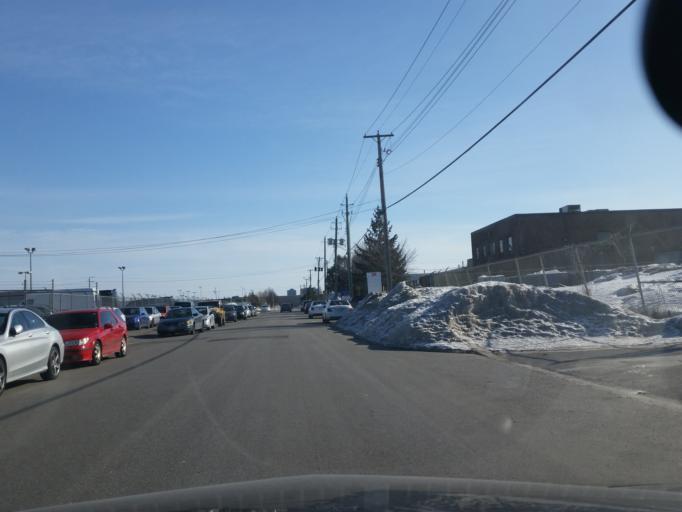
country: CA
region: Ontario
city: Ottawa
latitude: 45.3344
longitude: -75.7207
